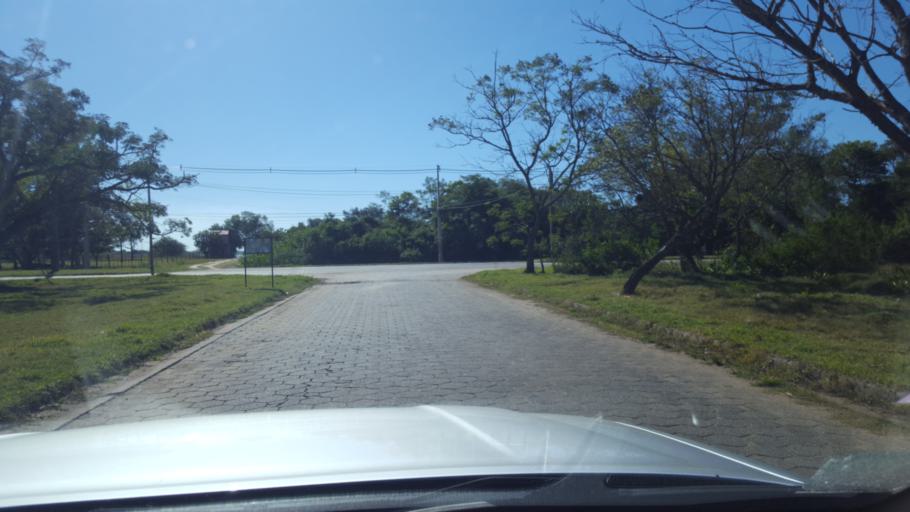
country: PY
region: Neembucu
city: Pilar
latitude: -26.8700
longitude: -58.3179
